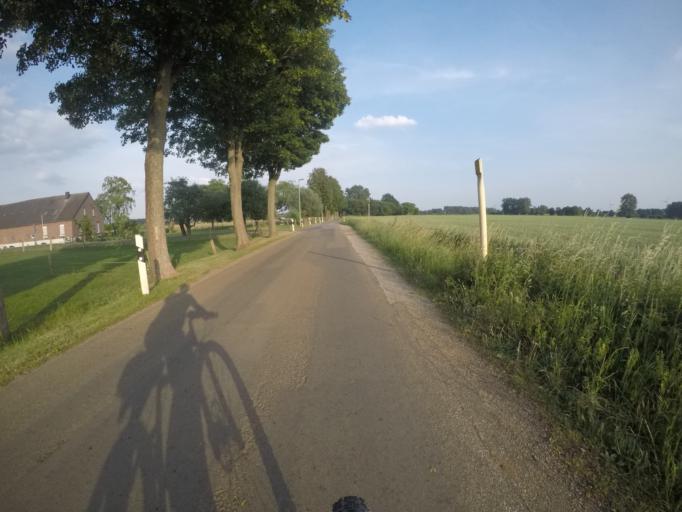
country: DE
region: North Rhine-Westphalia
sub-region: Regierungsbezirk Munster
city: Isselburg
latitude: 51.8261
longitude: 6.4767
